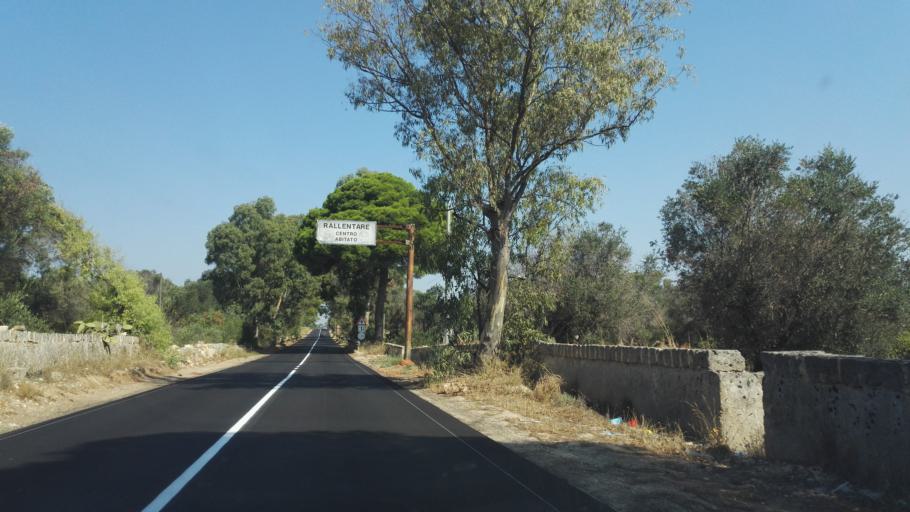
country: IT
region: Apulia
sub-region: Provincia di Lecce
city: Nardo
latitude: 40.1987
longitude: 17.9604
